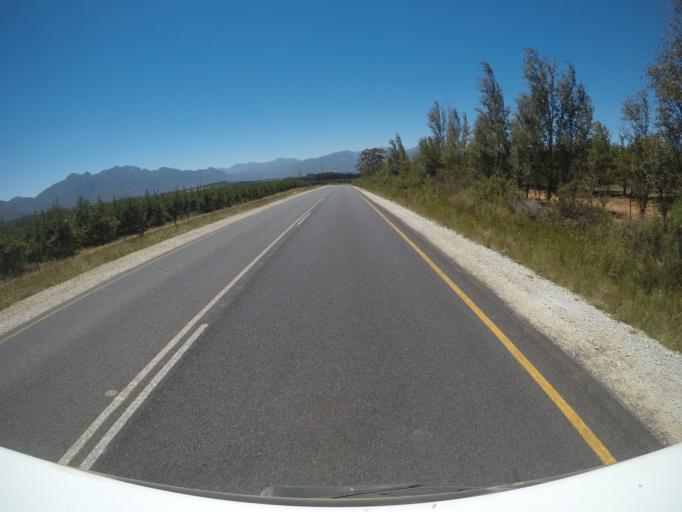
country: ZA
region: Western Cape
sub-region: Overberg District Municipality
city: Grabouw
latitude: -34.0612
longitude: 19.1357
